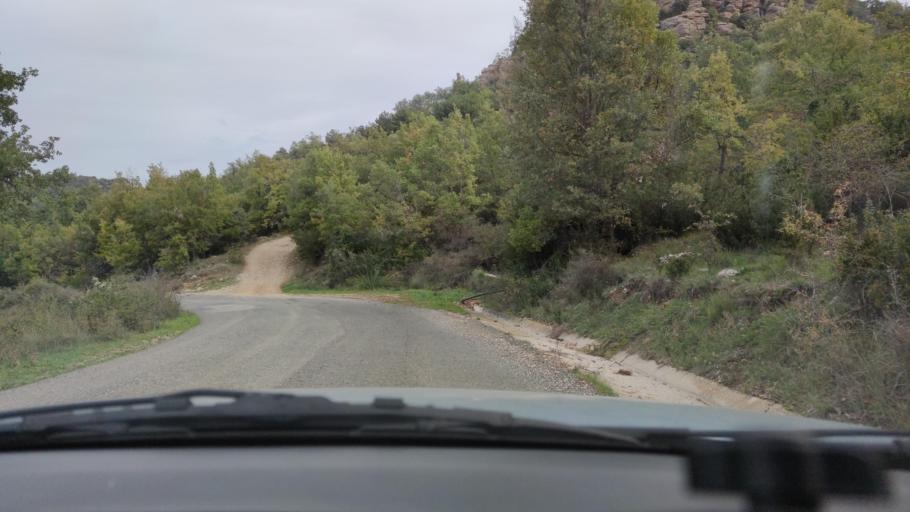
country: ES
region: Catalonia
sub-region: Provincia de Lleida
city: Llimiana
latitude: 42.0427
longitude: 1.0015
